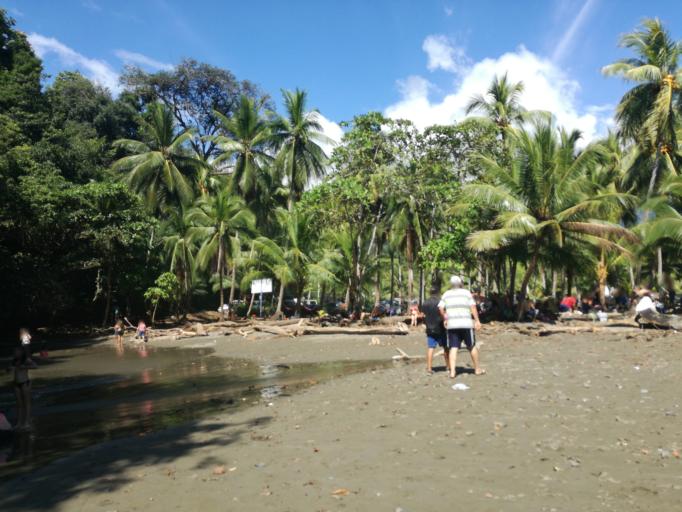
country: CR
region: San Jose
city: Mercedes
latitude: 9.0915
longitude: -83.6780
